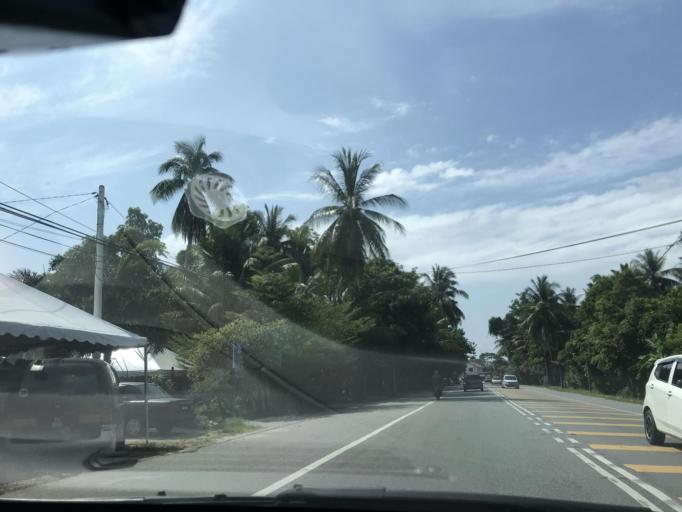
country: MY
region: Kelantan
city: Tumpat
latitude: 6.1369
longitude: 102.1724
